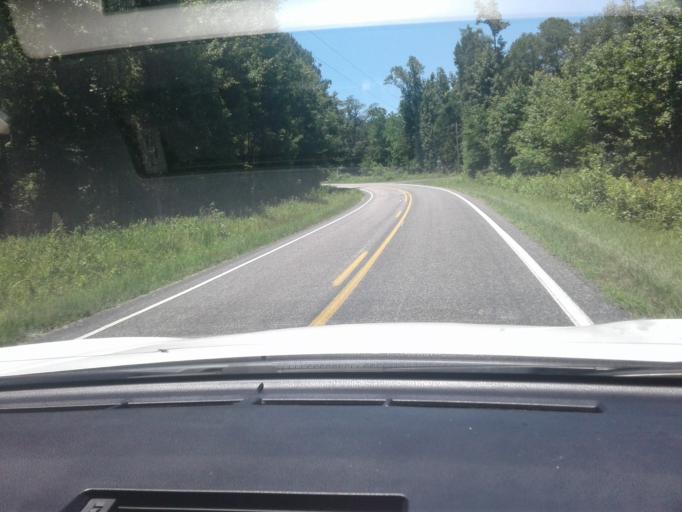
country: US
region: North Carolina
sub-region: Harnett County
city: Lillington
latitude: 35.3466
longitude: -78.9074
